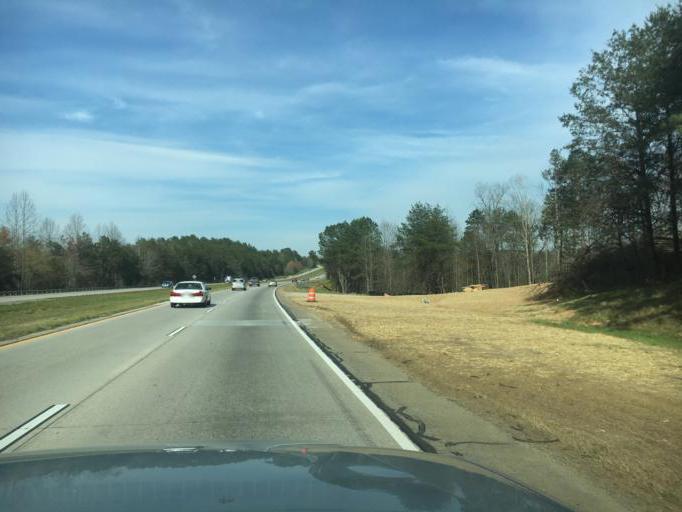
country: US
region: Georgia
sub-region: Hall County
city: Lula
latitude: 34.3746
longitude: -83.7236
